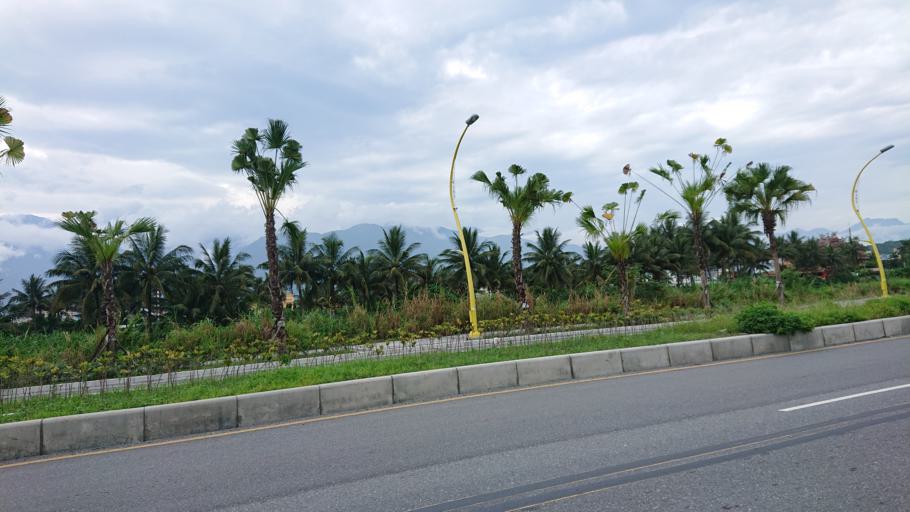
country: TW
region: Taiwan
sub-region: Hualien
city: Hualian
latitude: 23.9679
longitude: 121.6097
